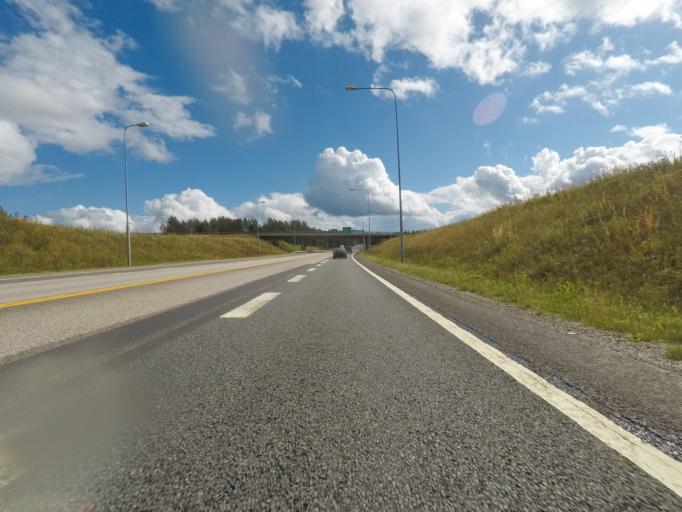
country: FI
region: Paijanne Tavastia
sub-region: Lahti
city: Heinola
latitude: 61.2964
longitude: 26.0701
